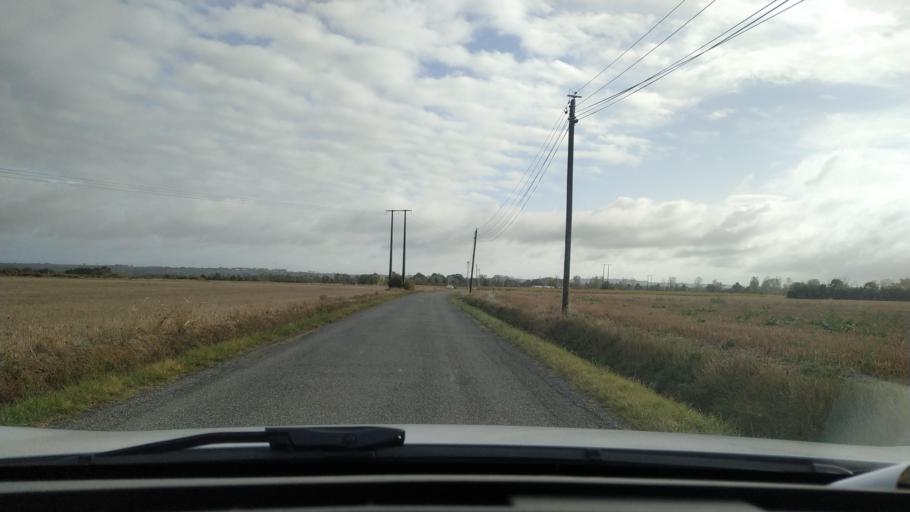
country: FR
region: Midi-Pyrenees
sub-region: Departement de la Haute-Garonne
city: Gaillac-Toulza
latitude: 43.2793
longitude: 1.5021
